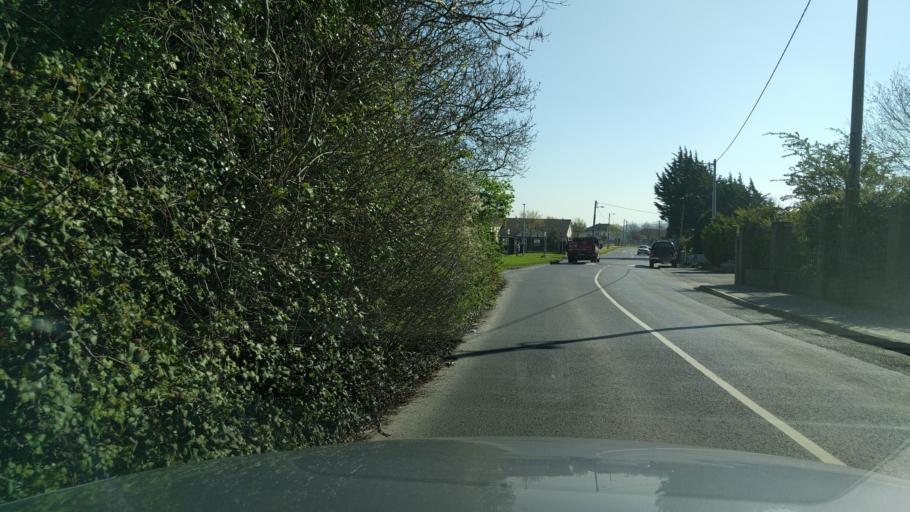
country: IE
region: Leinster
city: Firhouse
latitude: 53.2717
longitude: -6.3480
